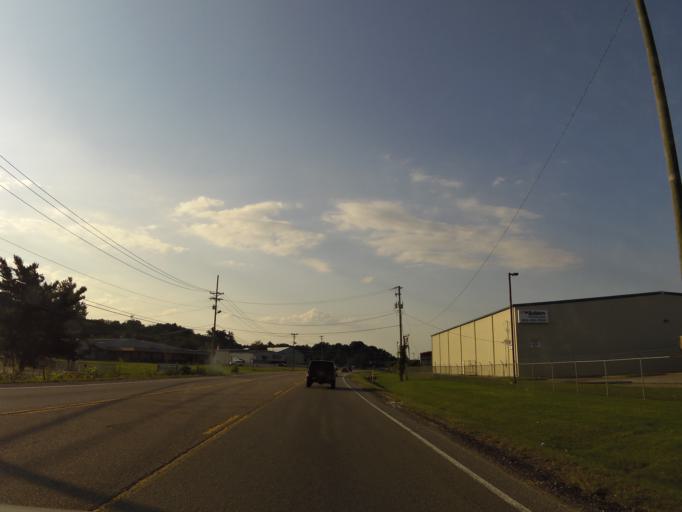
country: US
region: Tennessee
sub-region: Knox County
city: Knoxville
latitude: 35.9634
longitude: -83.8257
